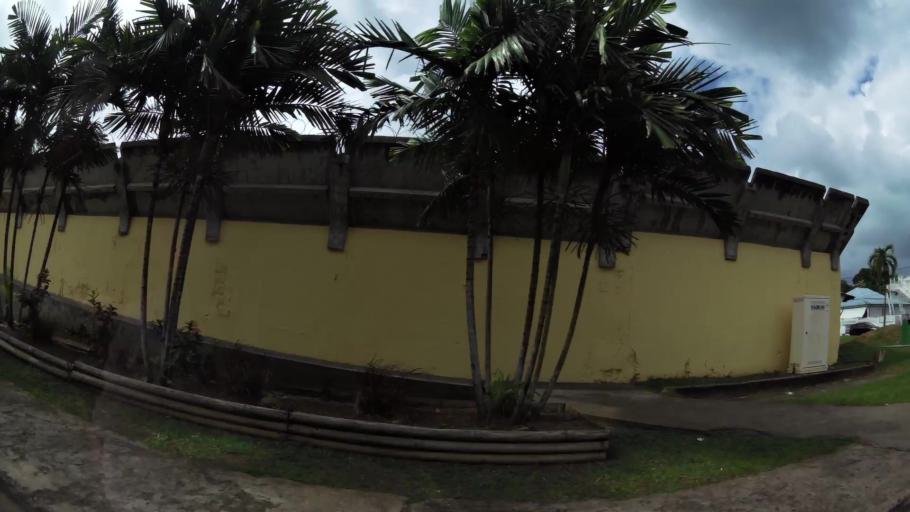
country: GP
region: Guadeloupe
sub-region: Guadeloupe
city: Baie-Mahault
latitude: 16.2650
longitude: -61.5889
